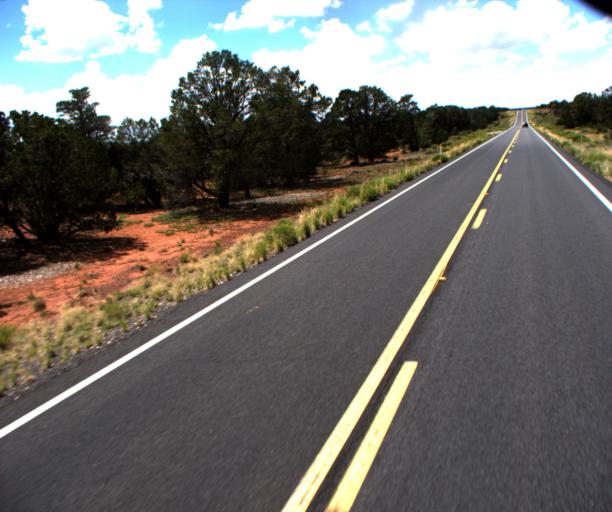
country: US
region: Arizona
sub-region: Coconino County
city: Parks
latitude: 35.5971
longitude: -112.0129
